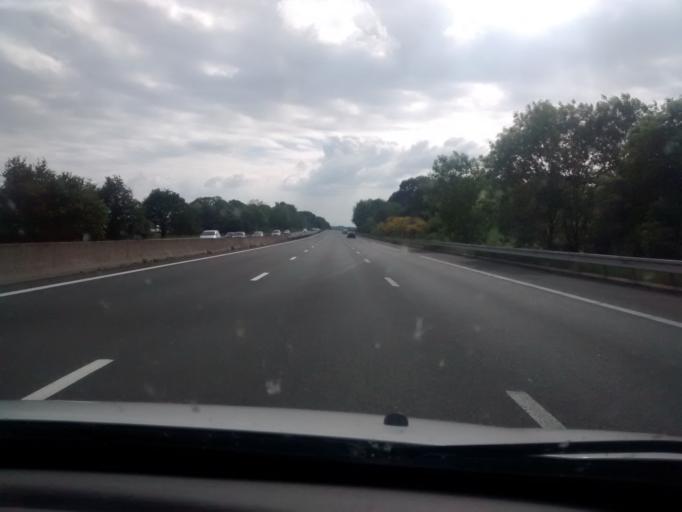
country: FR
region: Centre
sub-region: Departement d'Eure-et-Loir
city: Authon-du-Perche
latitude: 48.1988
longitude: 0.8753
